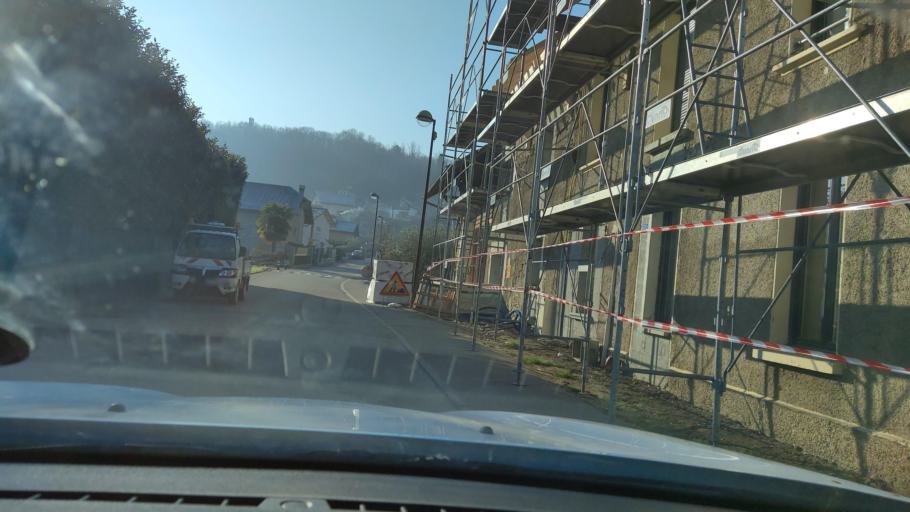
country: FR
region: Rhone-Alpes
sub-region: Departement de la Savoie
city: Viviers-du-Lac
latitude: 45.6440
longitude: 5.9042
